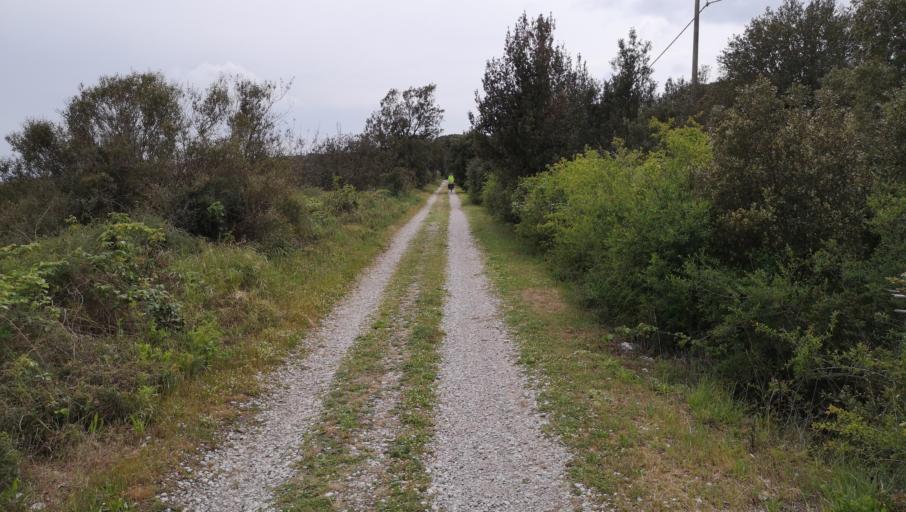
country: IT
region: Emilia-Romagna
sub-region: Provincia di Ferrara
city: Goro
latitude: 44.8263
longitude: 12.2671
